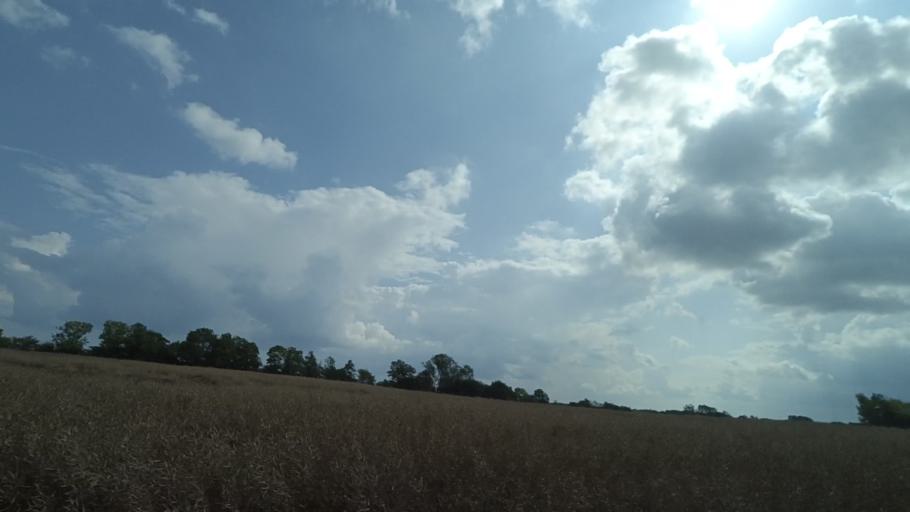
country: DK
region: Central Jutland
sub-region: Norddjurs Kommune
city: Allingabro
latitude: 56.5440
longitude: 10.3633
